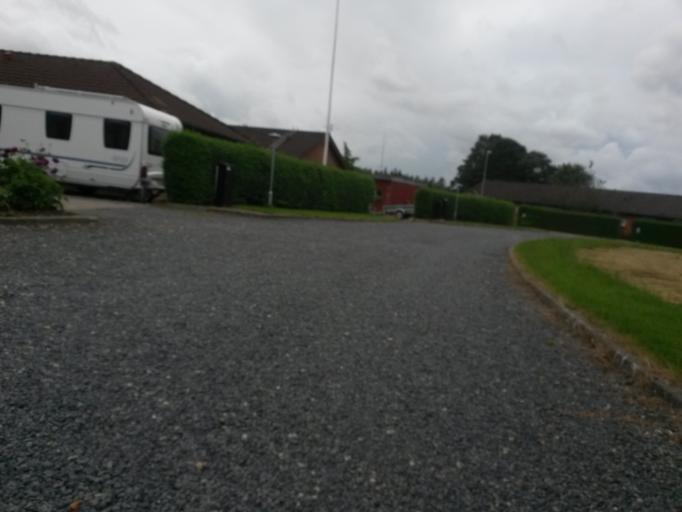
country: DK
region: Central Jutland
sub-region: Silkeborg Kommune
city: Kjellerup
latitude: 56.3253
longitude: 9.3370
